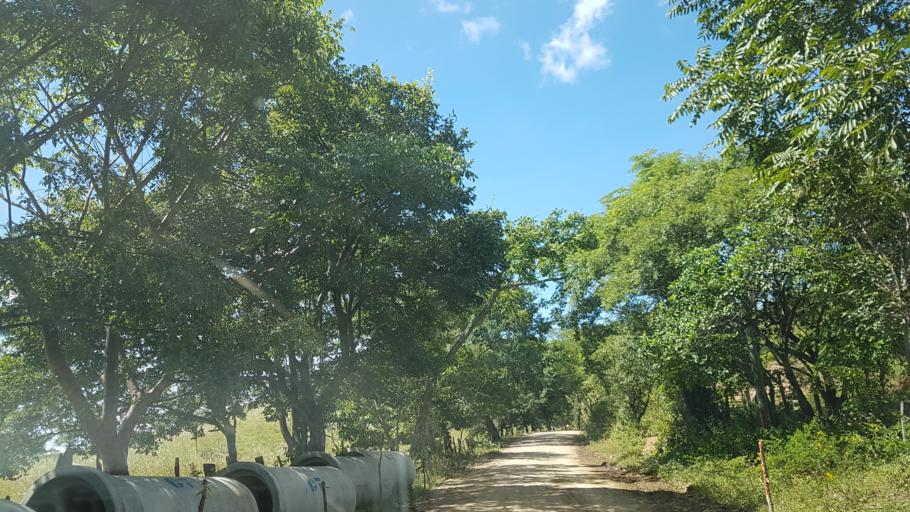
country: HN
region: El Paraiso
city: Santa Cruz
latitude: 13.7327
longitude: -86.6934
